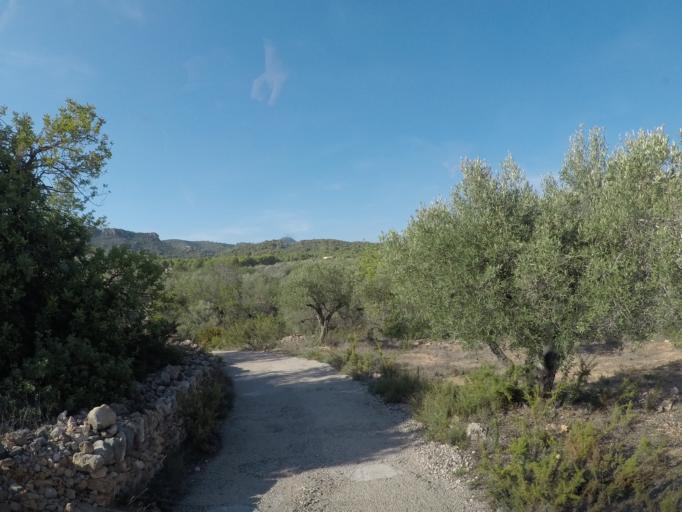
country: ES
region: Catalonia
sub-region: Provincia de Tarragona
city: El Perello
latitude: 40.9178
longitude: 0.7236
